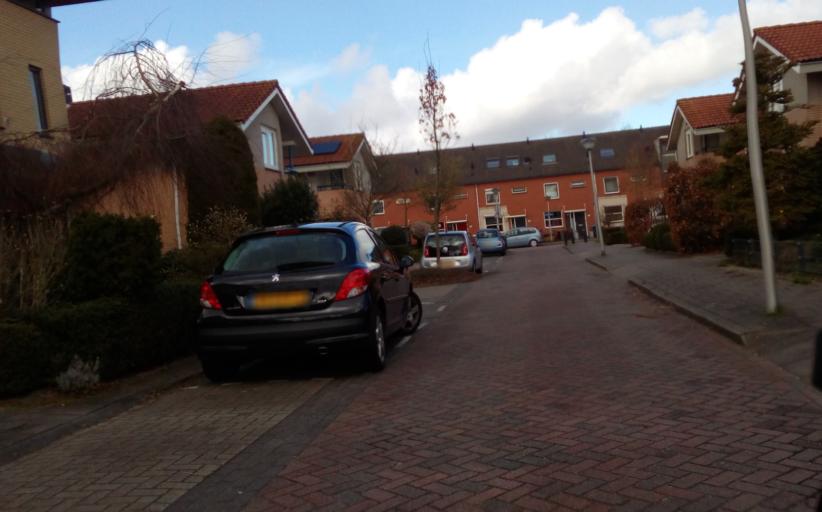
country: NL
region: South Holland
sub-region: Gemeente Lansingerland
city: Bergschenhoek
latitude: 51.9924
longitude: 4.5085
